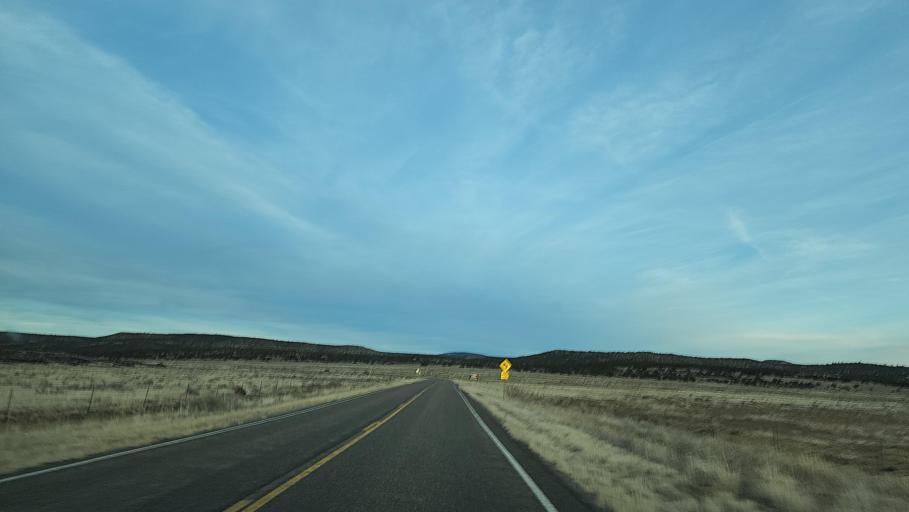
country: US
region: New Mexico
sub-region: Cibola County
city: Grants
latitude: 34.7101
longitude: -107.9938
